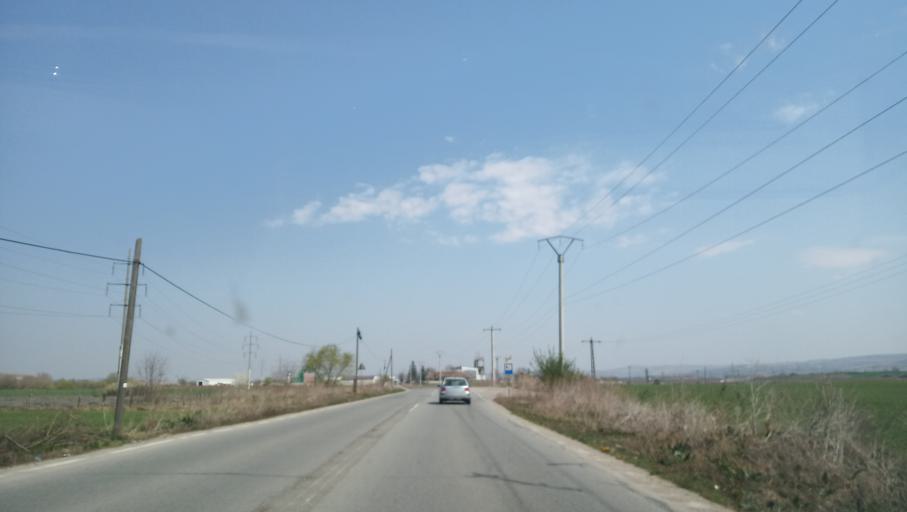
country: RO
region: Alba
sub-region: Municipiul Sebes
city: Lancram
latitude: 46.0156
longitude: 23.5151
